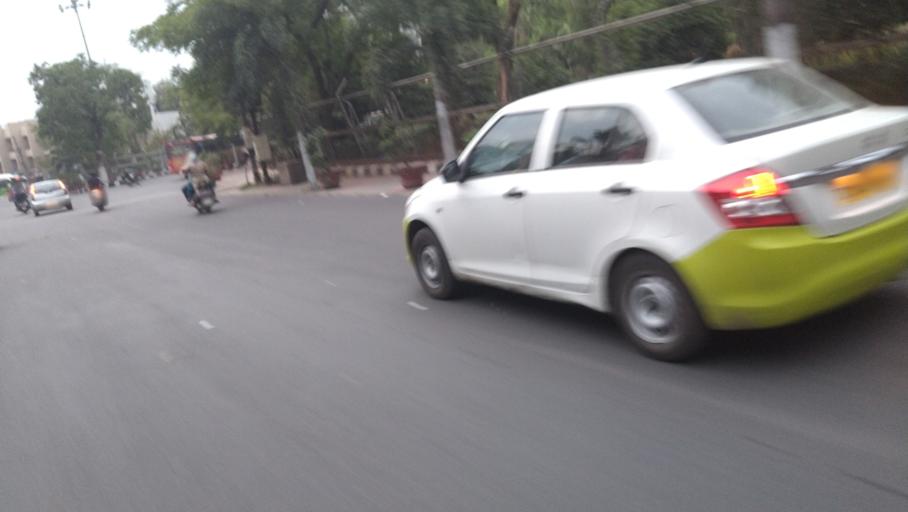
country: IN
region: Telangana
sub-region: Hyderabad
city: Malkajgiri
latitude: 17.4405
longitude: 78.4984
